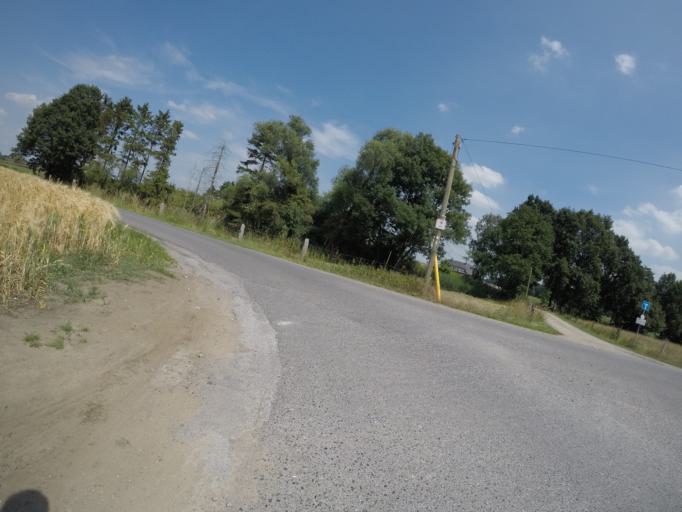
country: DE
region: North Rhine-Westphalia
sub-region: Regierungsbezirk Dusseldorf
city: Bocholt
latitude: 51.8221
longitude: 6.6457
